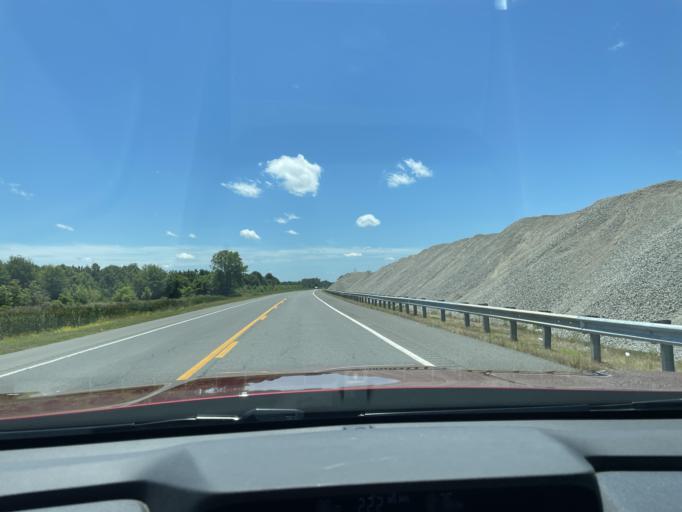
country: US
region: Arkansas
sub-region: Jefferson County
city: Pine Bluff
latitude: 34.1595
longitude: -91.9827
